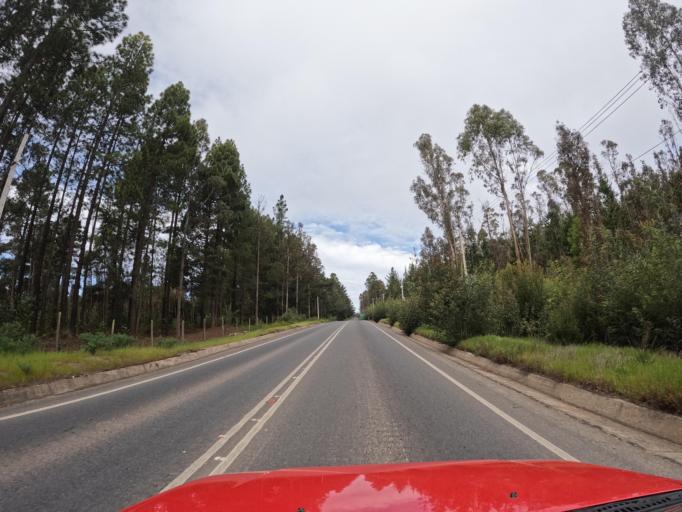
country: CL
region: O'Higgins
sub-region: Provincia de Colchagua
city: Santa Cruz
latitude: -34.3571
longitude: -71.8766
